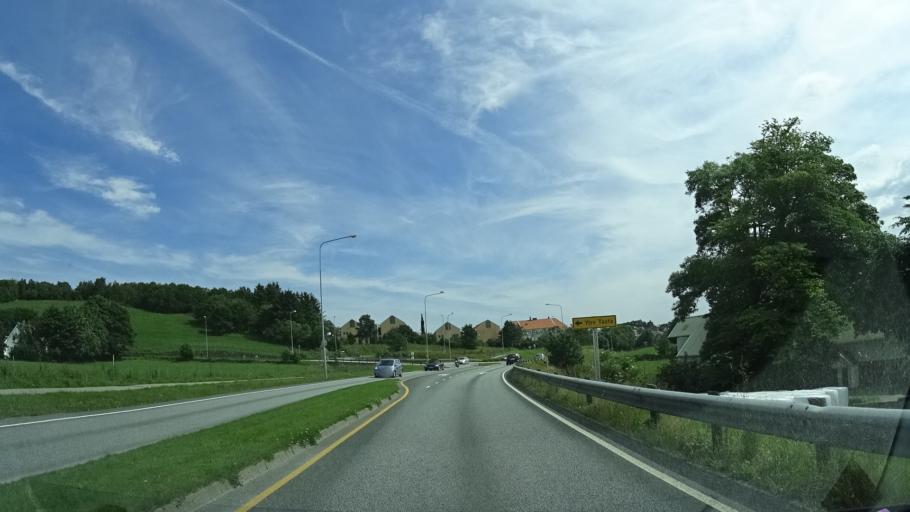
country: NO
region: Rogaland
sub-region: Randaberg
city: Randaberg
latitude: 58.9836
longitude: 5.6748
